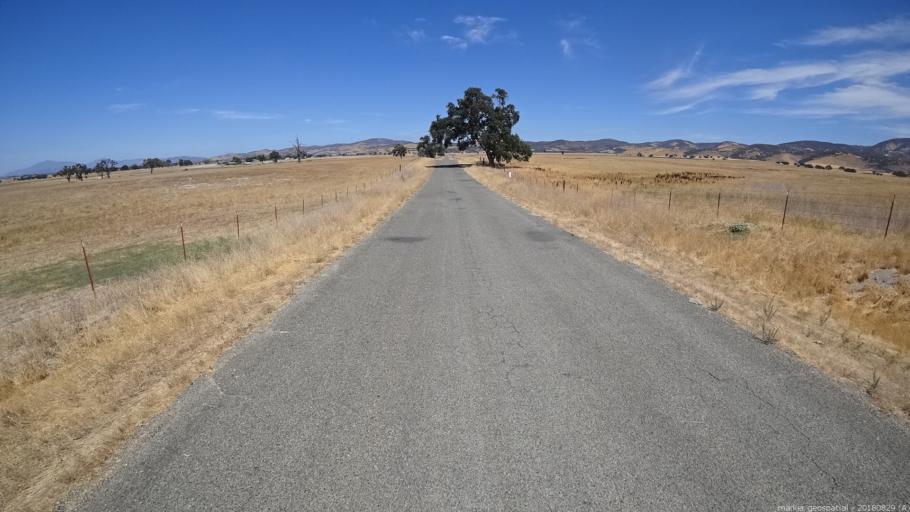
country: US
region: California
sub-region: San Luis Obispo County
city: Lake Nacimiento
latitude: 35.9264
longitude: -121.0643
